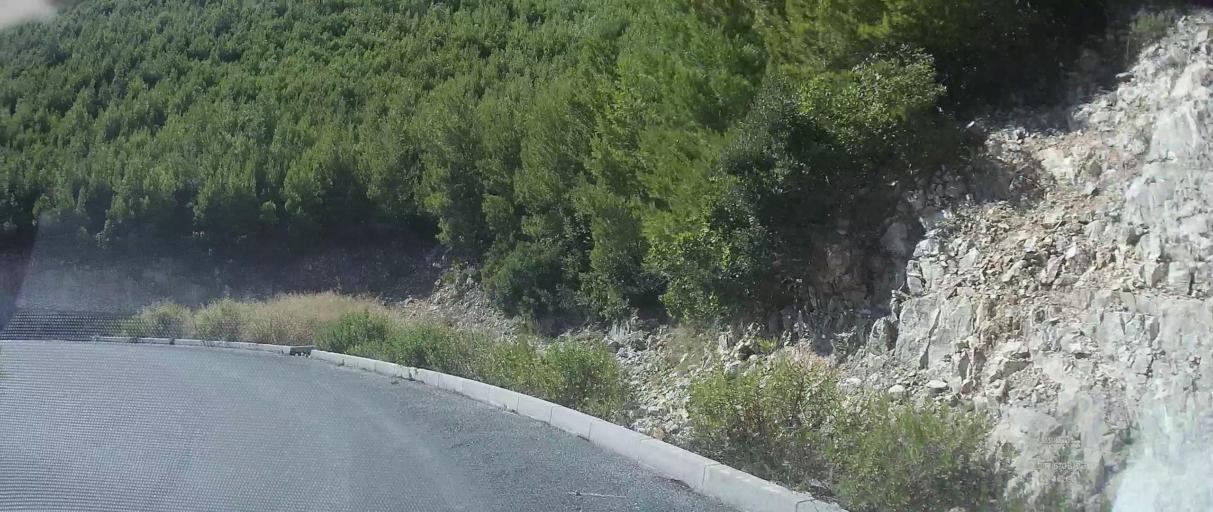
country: HR
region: Dubrovacko-Neretvanska
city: Blato
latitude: 42.7366
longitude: 17.5148
